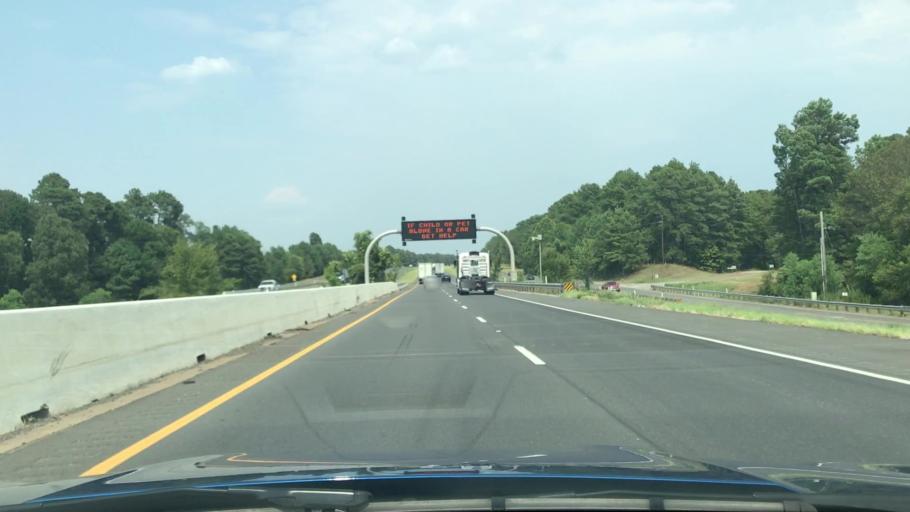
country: US
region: Texas
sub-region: Gregg County
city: Longview
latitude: 32.4531
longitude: -94.7003
